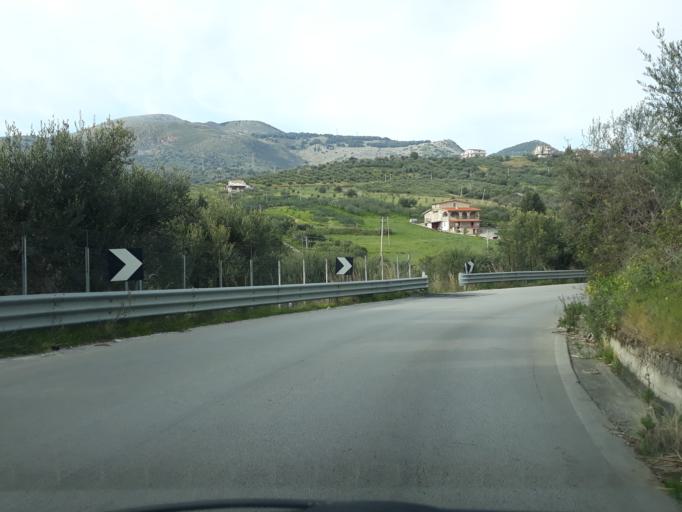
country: IT
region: Sicily
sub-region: Palermo
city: Giardinello
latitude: 38.0734
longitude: 13.1530
